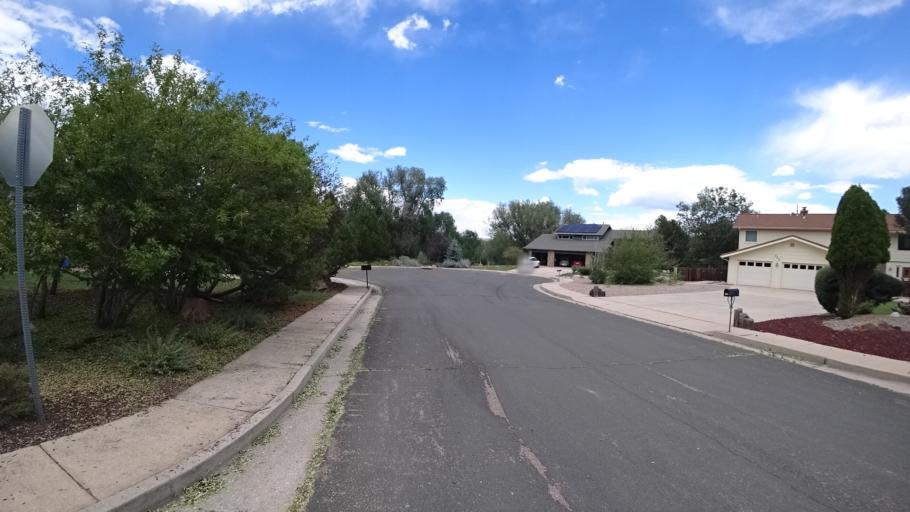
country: US
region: Colorado
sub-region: El Paso County
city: Colorado Springs
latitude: 38.7914
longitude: -104.8316
